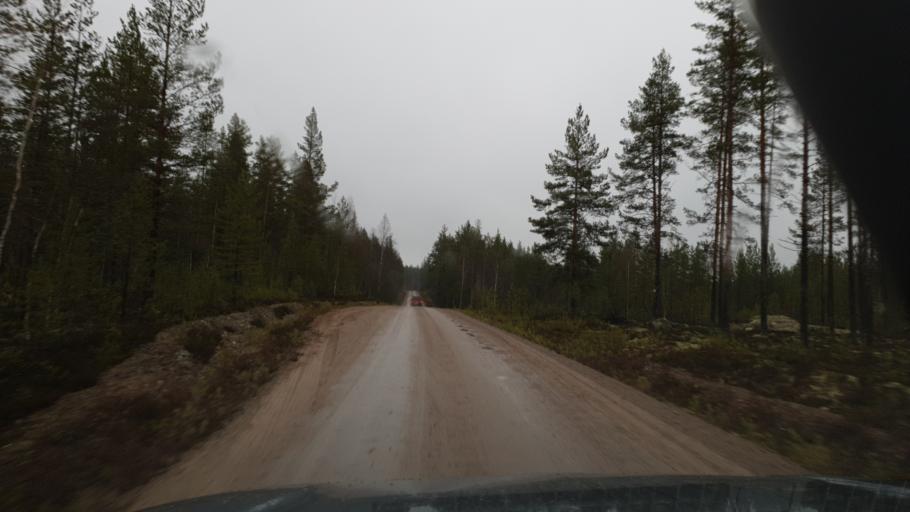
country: SE
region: Vaesternorrland
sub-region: Ange Kommun
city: Ange
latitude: 62.2165
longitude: 15.5202
